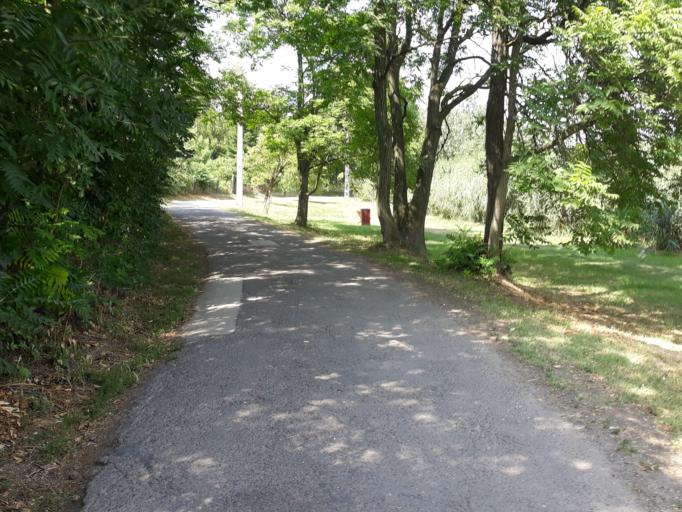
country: HU
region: Bekes
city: Oroshaza
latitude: 46.5629
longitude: 20.6247
